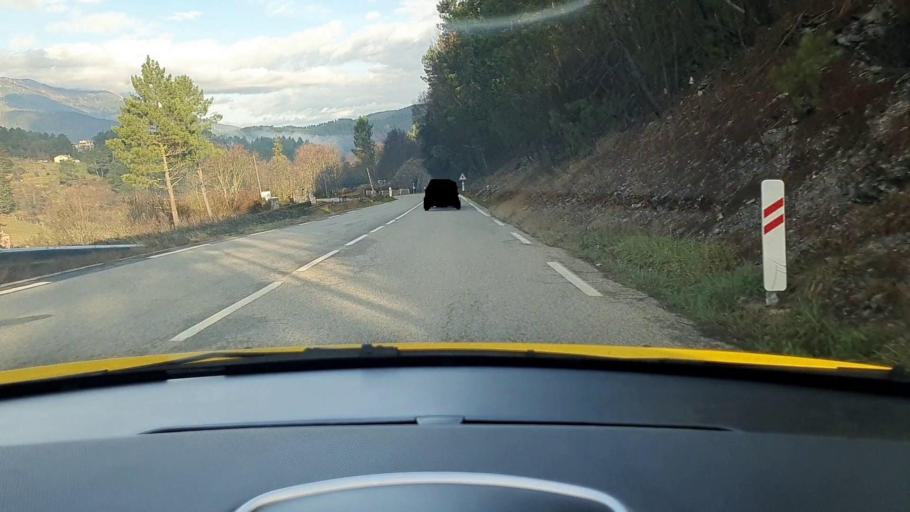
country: FR
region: Languedoc-Roussillon
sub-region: Departement du Gard
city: Branoux-les-Taillades
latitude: 44.2951
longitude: 3.9787
